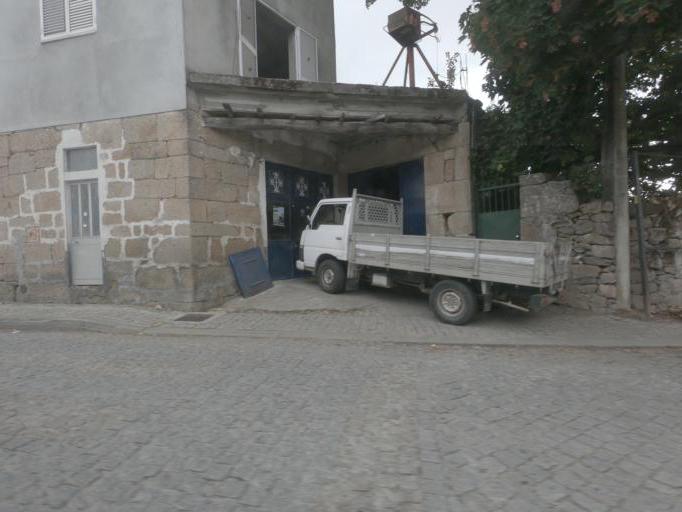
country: PT
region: Vila Real
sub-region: Sabrosa
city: Sabrosa
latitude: 41.2914
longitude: -7.5214
